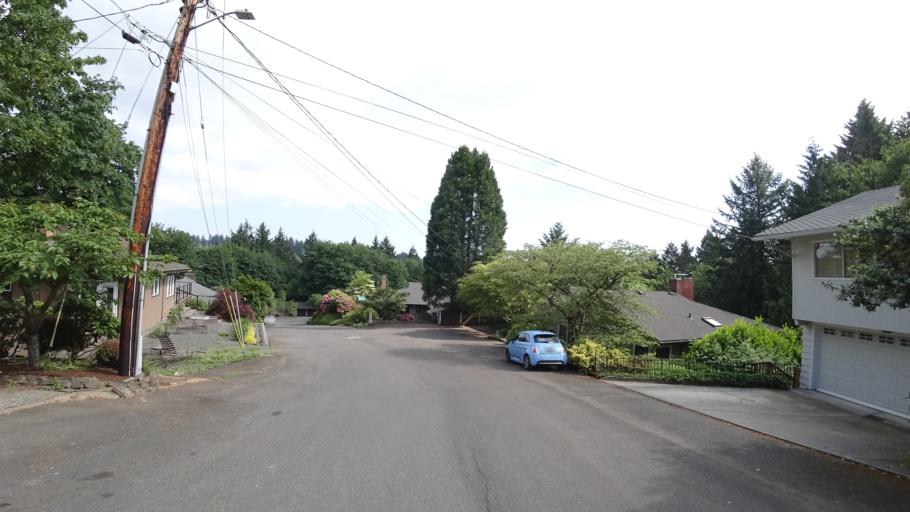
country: US
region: Oregon
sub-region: Multnomah County
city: Portland
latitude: 45.5047
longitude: -122.7118
